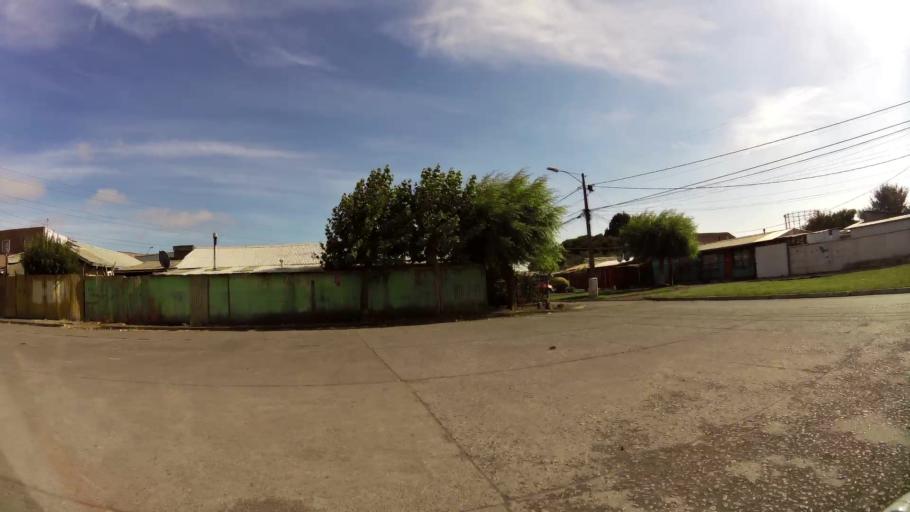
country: CL
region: Biobio
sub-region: Provincia de Concepcion
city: Talcahuano
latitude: -36.7783
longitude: -73.1148
